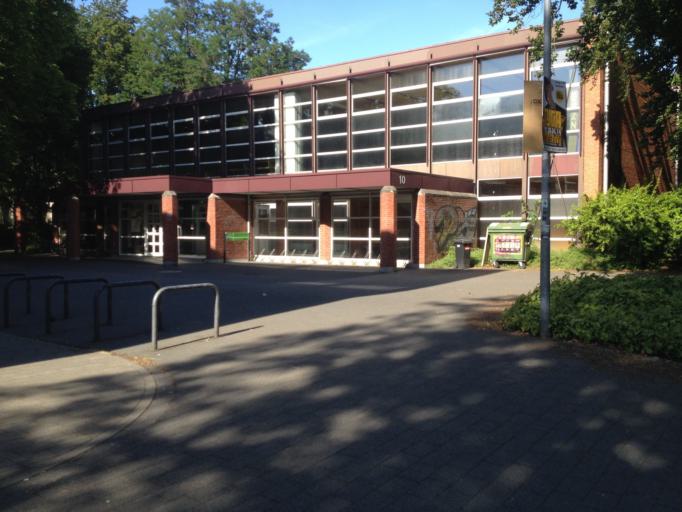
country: DE
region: Baden-Wuerttemberg
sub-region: Karlsruhe Region
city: Karlsruhe
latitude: 49.0145
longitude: 8.3942
